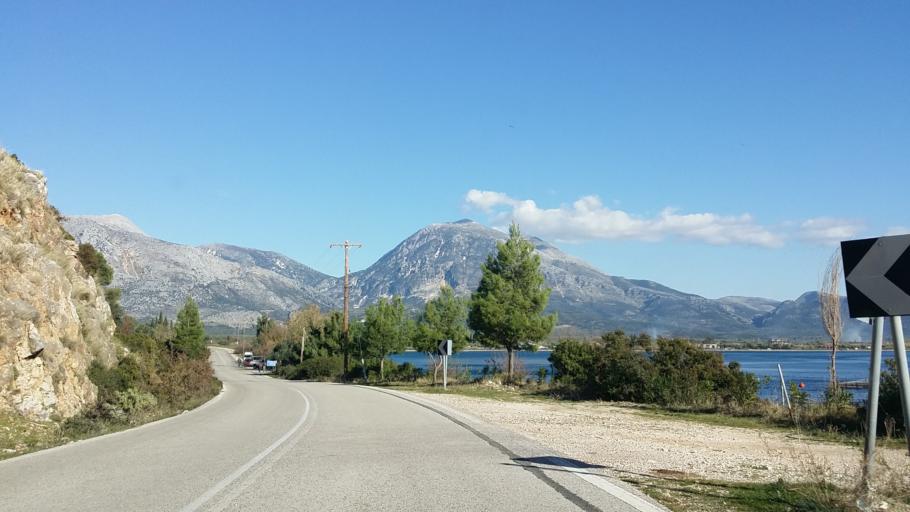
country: GR
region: West Greece
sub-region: Nomos Aitolias kai Akarnanias
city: Kandila
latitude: 38.6728
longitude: 20.9258
